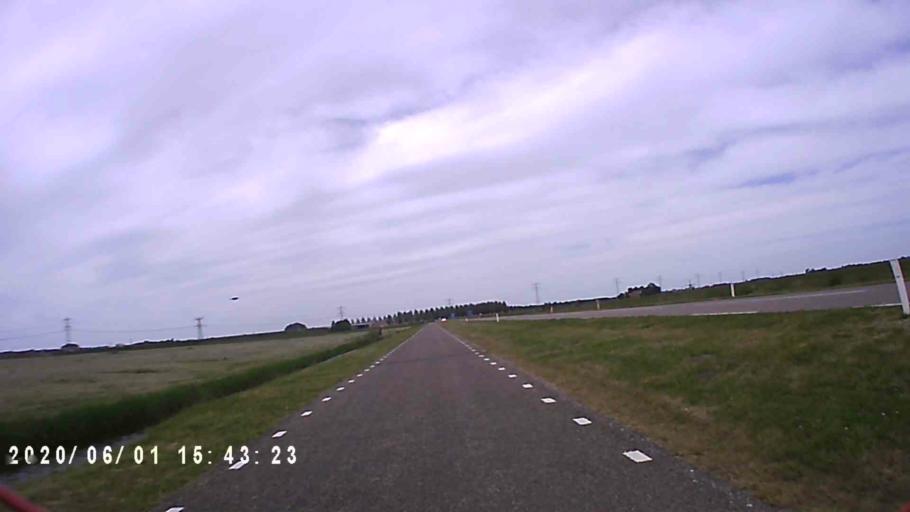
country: NL
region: Friesland
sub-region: Gemeente Boarnsterhim
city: Wergea
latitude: 53.1610
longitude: 5.8278
